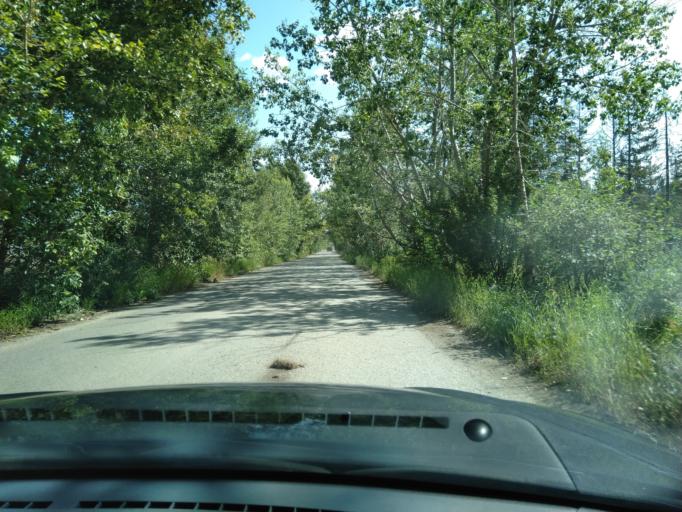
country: CA
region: Alberta
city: Calgary
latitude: 51.1019
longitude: -114.2242
